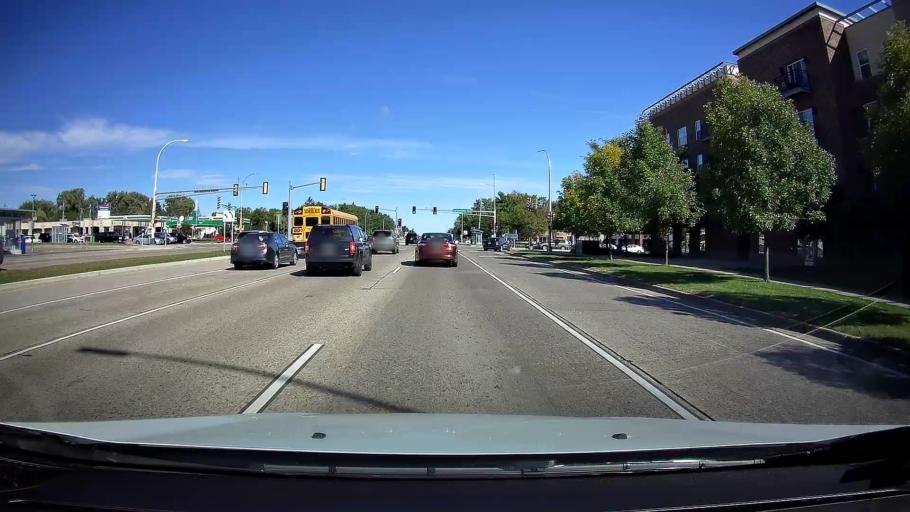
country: US
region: Minnesota
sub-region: Ramsey County
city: Falcon Heights
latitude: 44.9909
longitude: -93.1665
